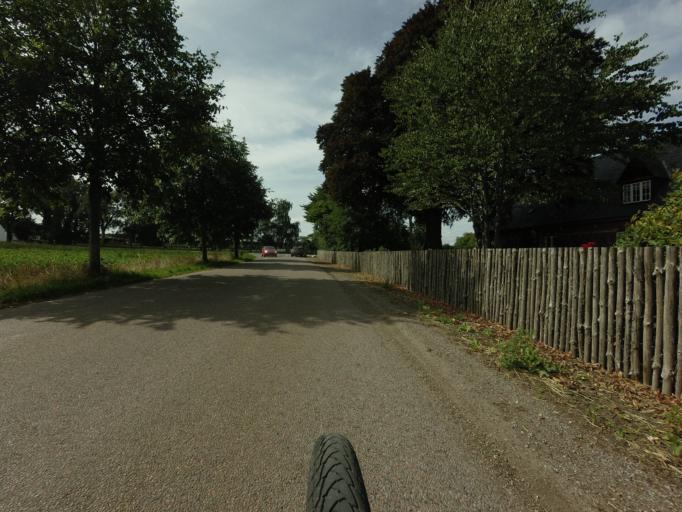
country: DK
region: Zealand
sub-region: Faxe Kommune
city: Fakse Ladeplads
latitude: 55.2527
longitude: 12.2248
